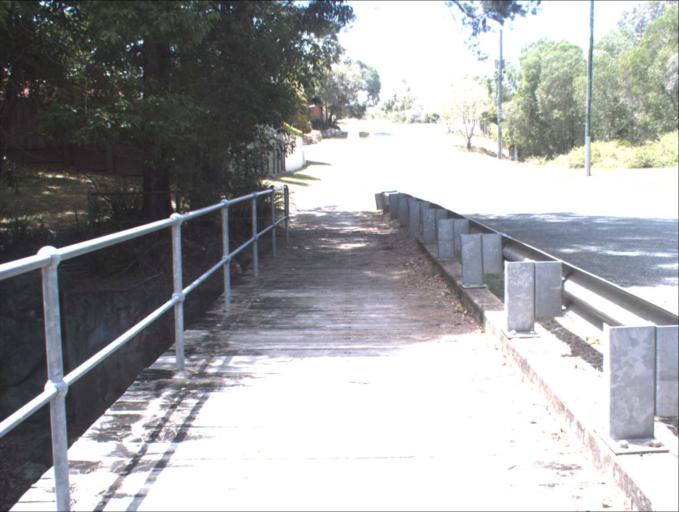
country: AU
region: Queensland
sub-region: Logan
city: Windaroo
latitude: -27.7402
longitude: 153.1856
